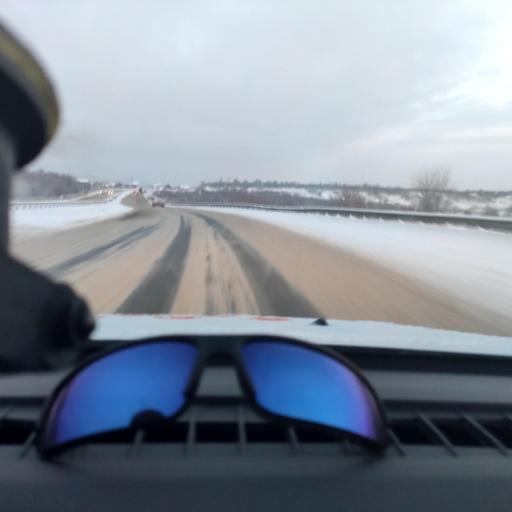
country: RU
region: Samara
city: Novokuybyshevsk
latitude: 53.0577
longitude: 50.0188
